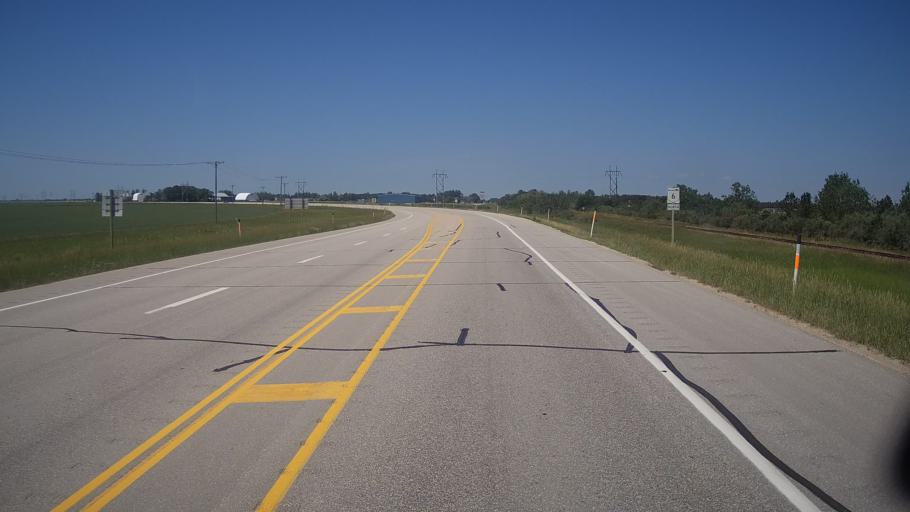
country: CA
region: Manitoba
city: Stonewall
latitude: 50.1209
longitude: -97.5293
